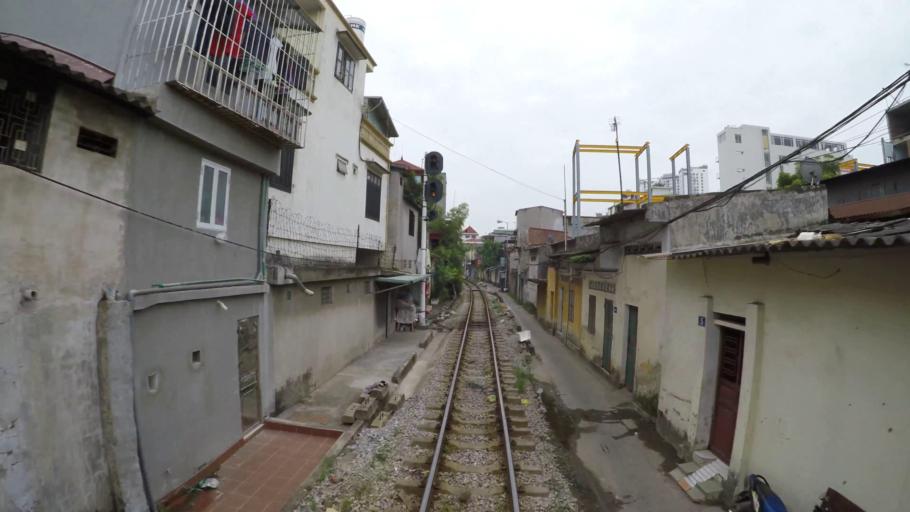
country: VN
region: Hai Phong
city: Haiphong
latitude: 20.8529
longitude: 106.6671
